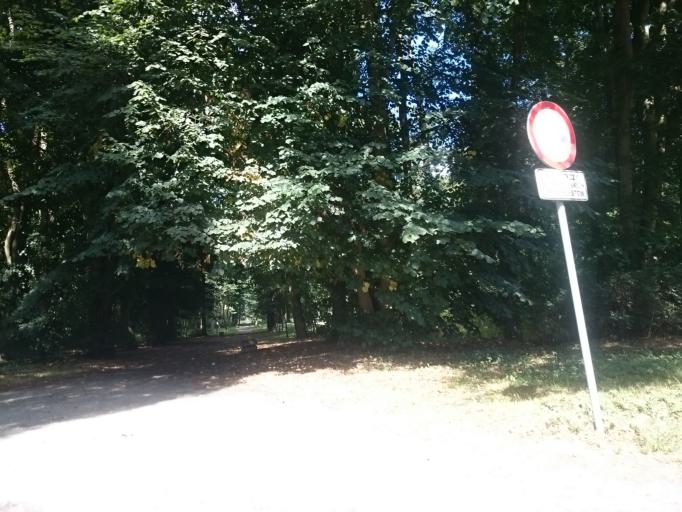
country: PL
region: West Pomeranian Voivodeship
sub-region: Swinoujscie
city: Swinoujscie
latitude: 53.9104
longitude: 14.2641
